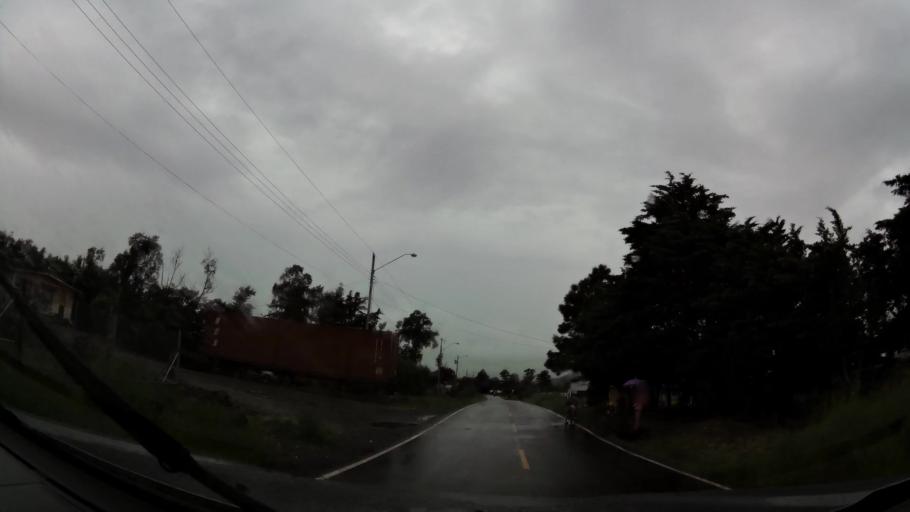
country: PA
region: Chiriqui
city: Volcan
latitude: 8.7944
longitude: -82.6472
